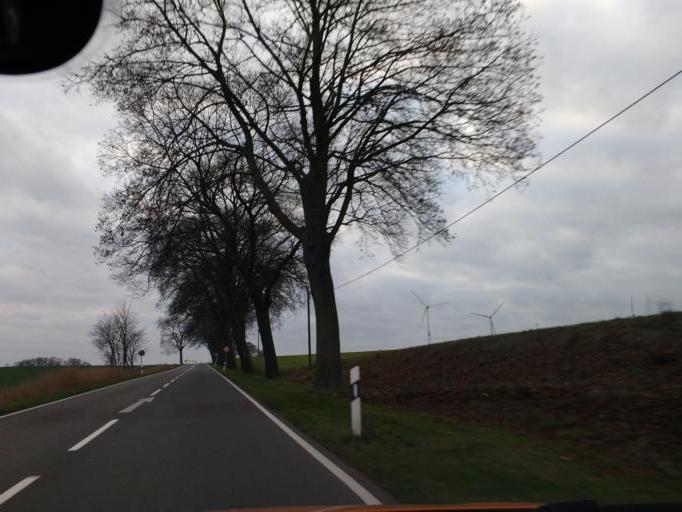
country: DE
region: Brandenburg
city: Wriezen
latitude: 52.6806
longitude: 14.0894
